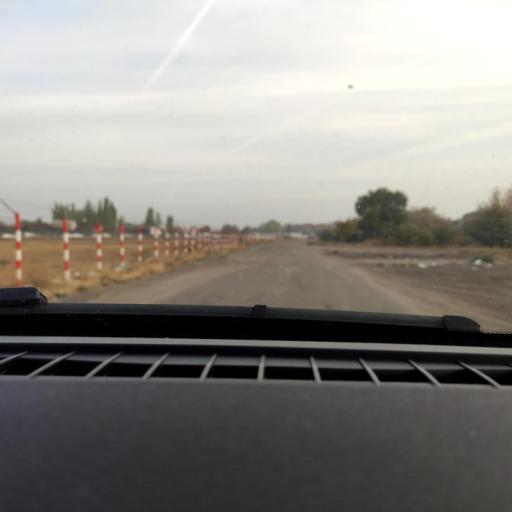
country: RU
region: Voronezj
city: Voronezh
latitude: 51.6617
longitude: 39.2687
